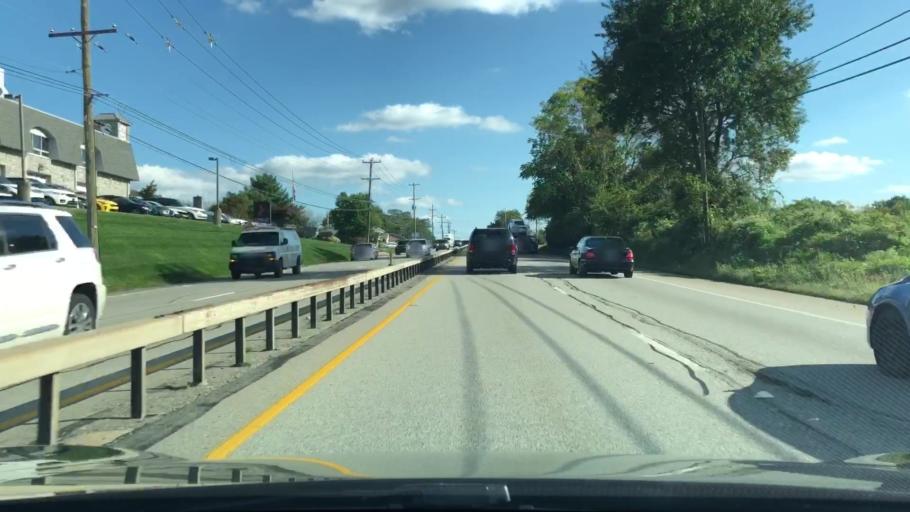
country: US
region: Pennsylvania
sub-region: Delaware County
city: Chester Heights
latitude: 39.8941
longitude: -75.5576
